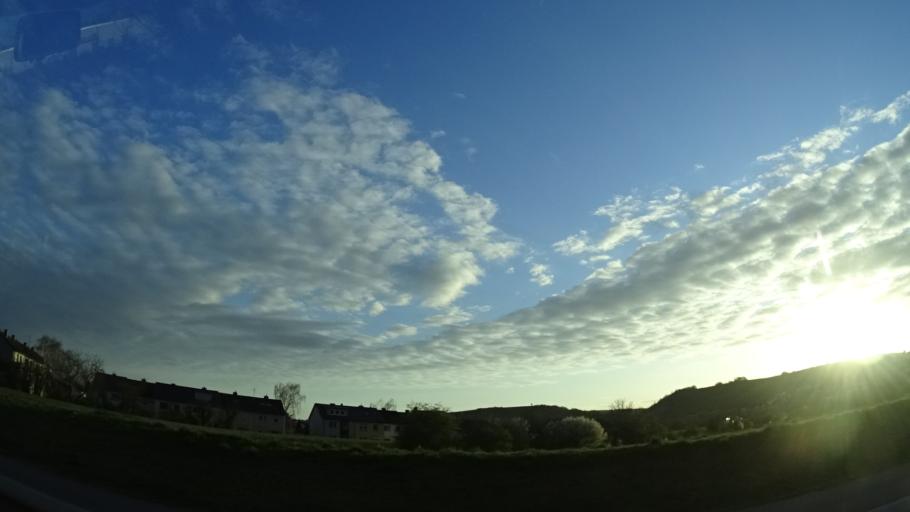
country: DE
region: Rheinland-Pfalz
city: Munster-Sarmsheim
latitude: 49.9420
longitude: 7.9087
